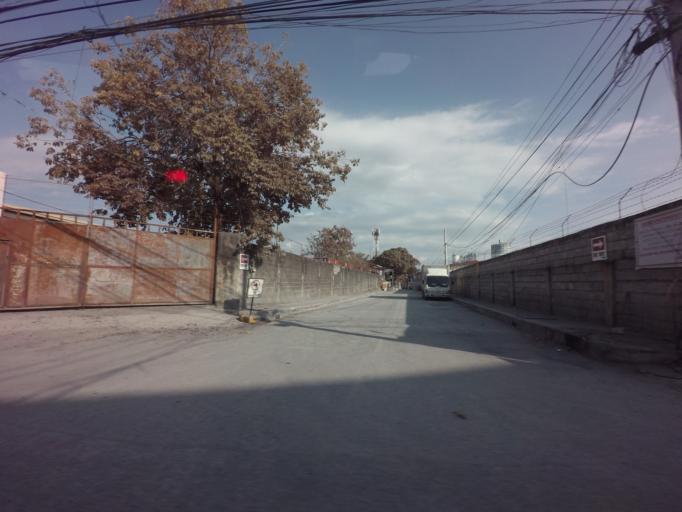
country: PH
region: Calabarzon
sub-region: Province of Rizal
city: Taguig
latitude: 14.4802
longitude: 121.0545
